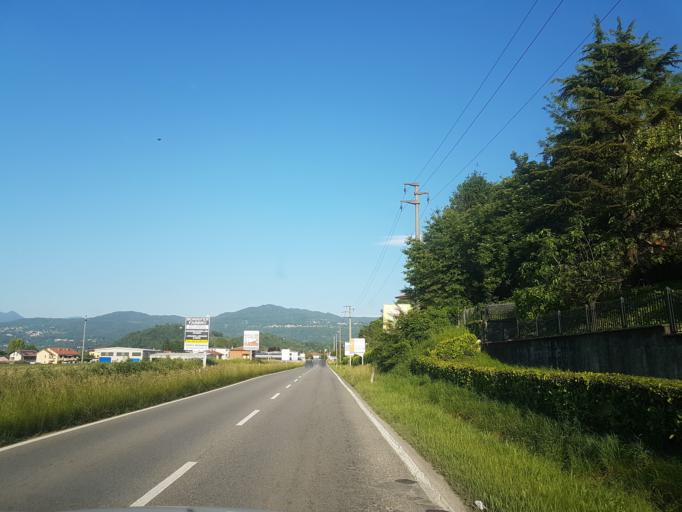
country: IT
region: Lombardy
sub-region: Provincia di Lecco
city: Garbagnate Monastero
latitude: 45.7755
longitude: 9.3007
